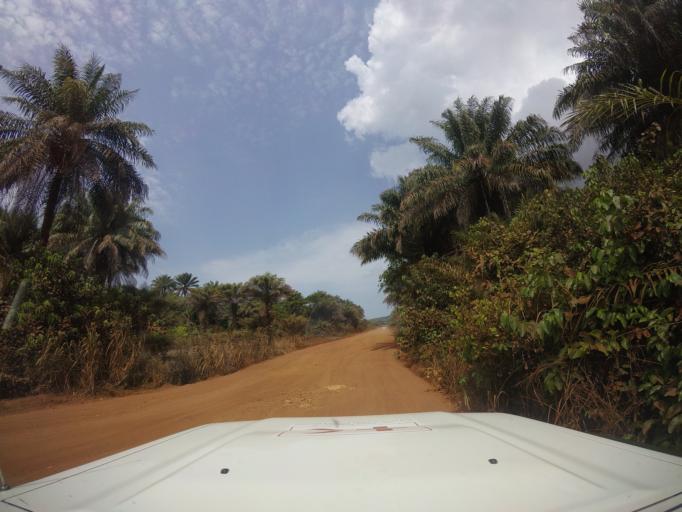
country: LR
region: Grand Cape Mount
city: Robertsport
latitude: 6.7034
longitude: -11.3220
